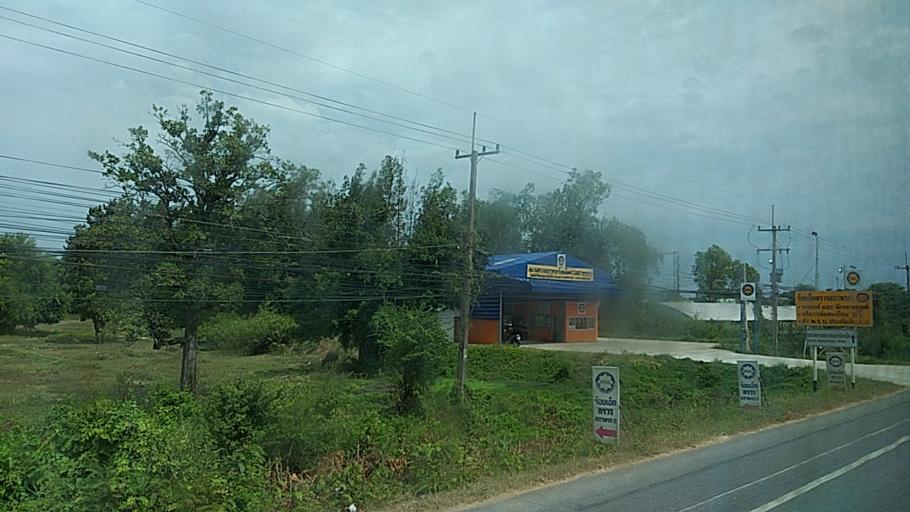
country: TH
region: Roi Et
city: Roi Et
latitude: 16.0725
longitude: 103.5968
